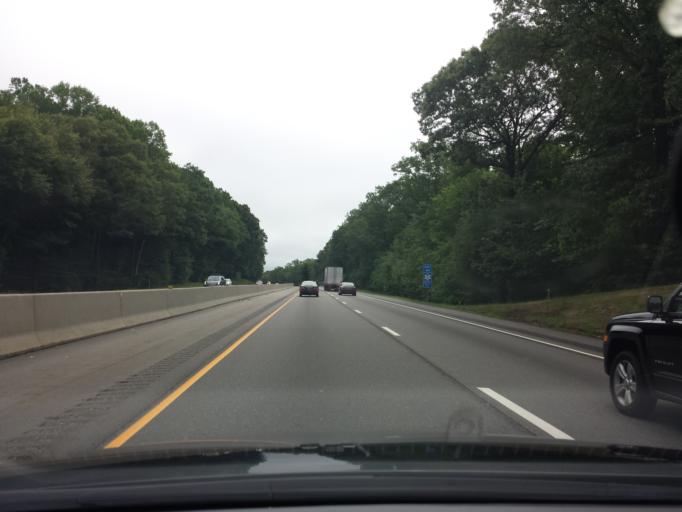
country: US
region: Connecticut
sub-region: Middlesex County
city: Westbrook Center
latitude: 41.2920
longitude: -72.4730
